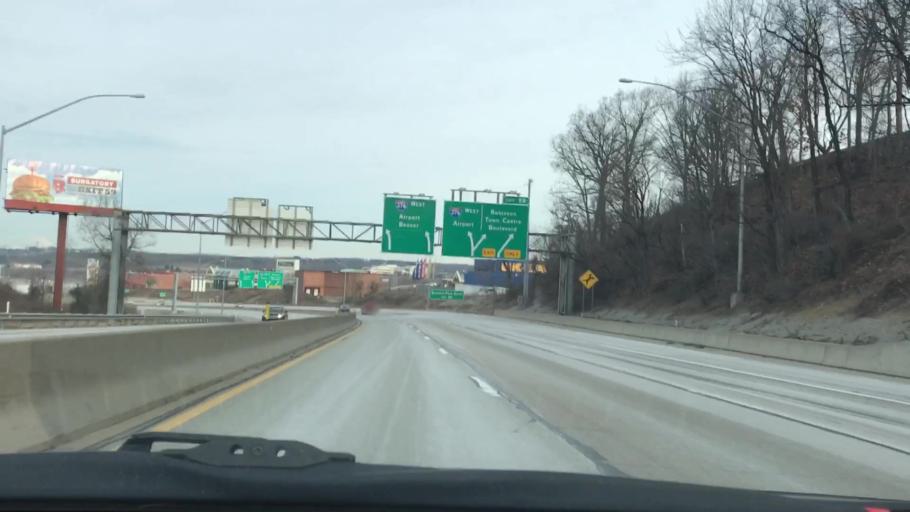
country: US
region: Pennsylvania
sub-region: Allegheny County
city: Oakdale
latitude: 40.4485
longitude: -80.1685
